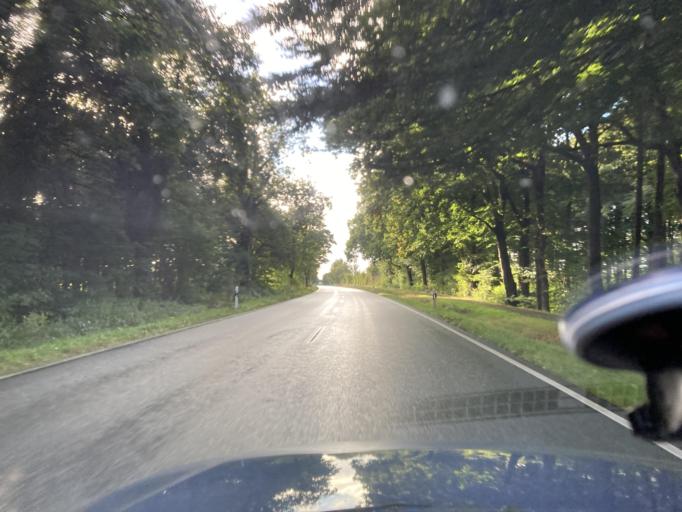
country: DE
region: Schleswig-Holstein
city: Nordhastedt
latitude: 54.1961
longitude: 9.1751
